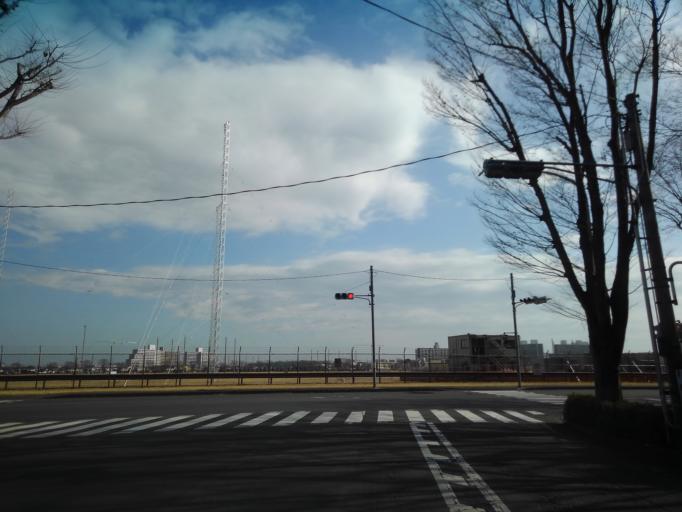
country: JP
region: Saitama
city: Tokorozawa
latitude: 35.8093
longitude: 139.4664
